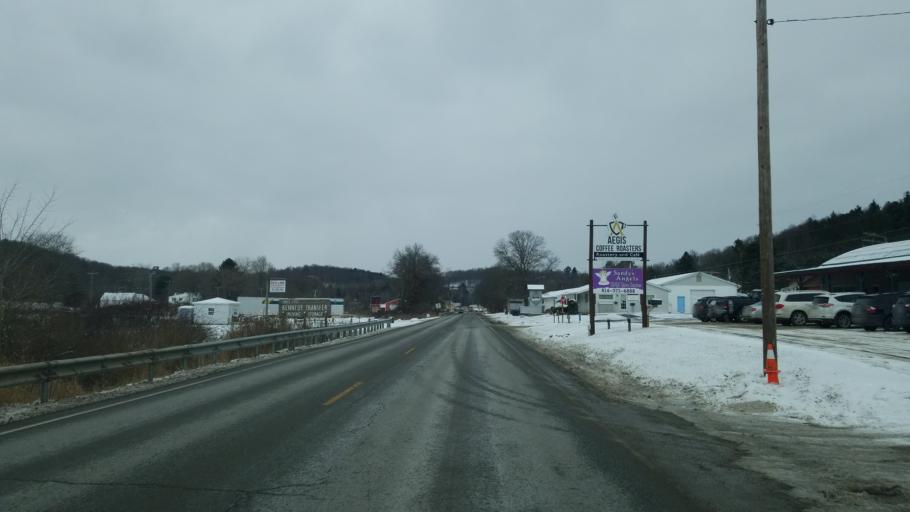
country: US
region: Pennsylvania
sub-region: Clearfield County
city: Sandy
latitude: 41.0878
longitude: -78.7670
